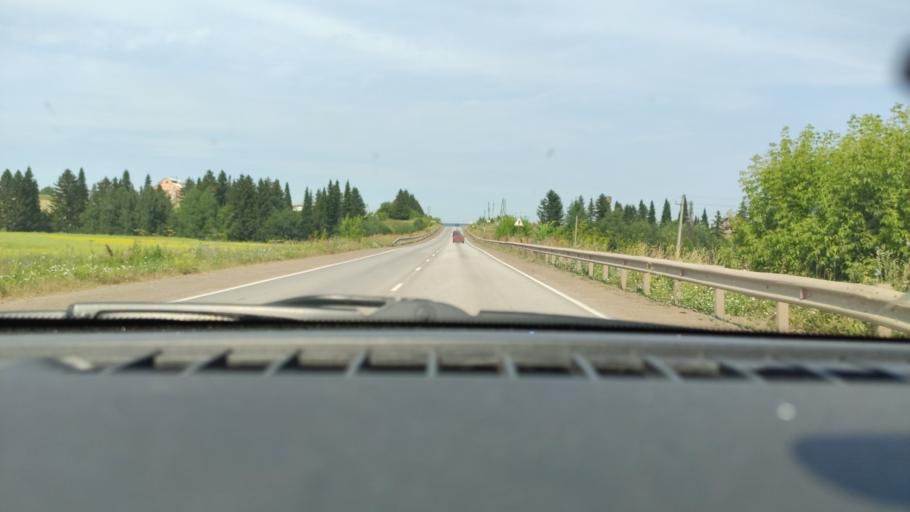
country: RU
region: Perm
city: Lobanovo
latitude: 57.8599
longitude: 56.2958
